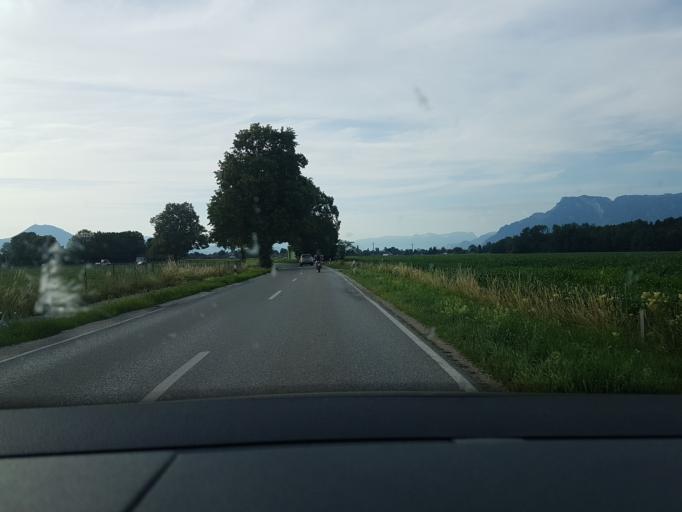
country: DE
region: Bavaria
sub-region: Upper Bavaria
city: Ainring
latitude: 47.8443
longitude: 12.9495
